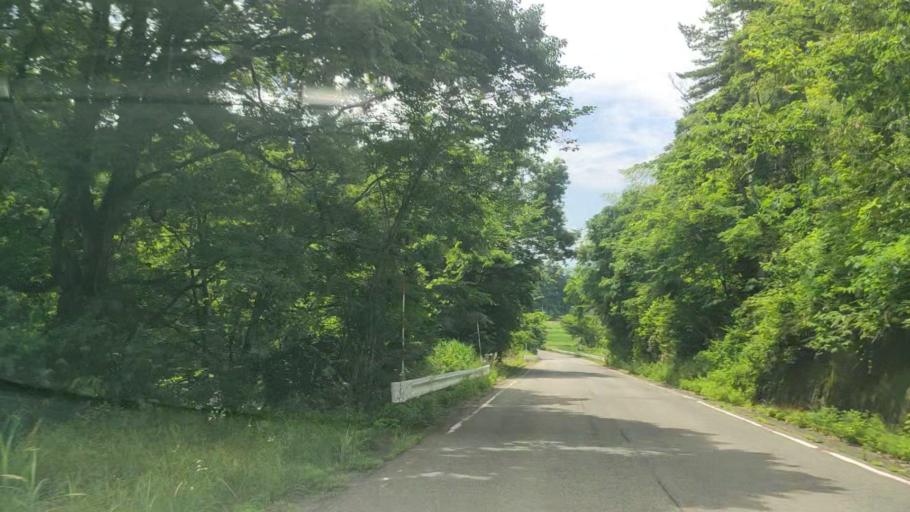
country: JP
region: Hyogo
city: Toyooka
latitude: 35.5077
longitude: 134.6853
